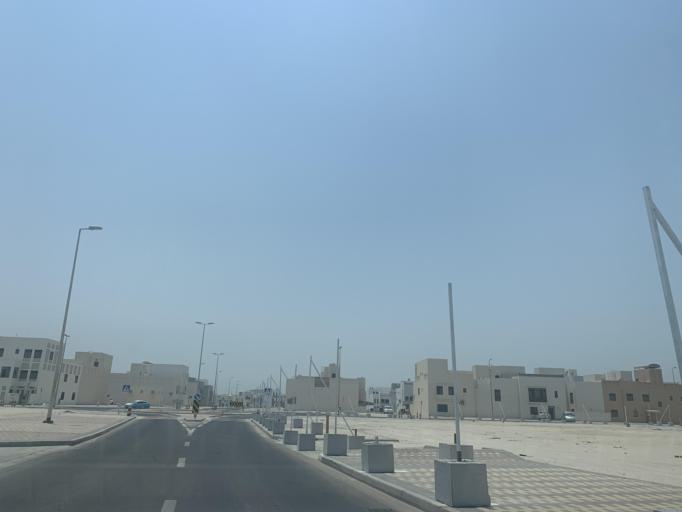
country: BH
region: Muharraq
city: Al Hadd
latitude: 26.2341
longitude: 50.6751
